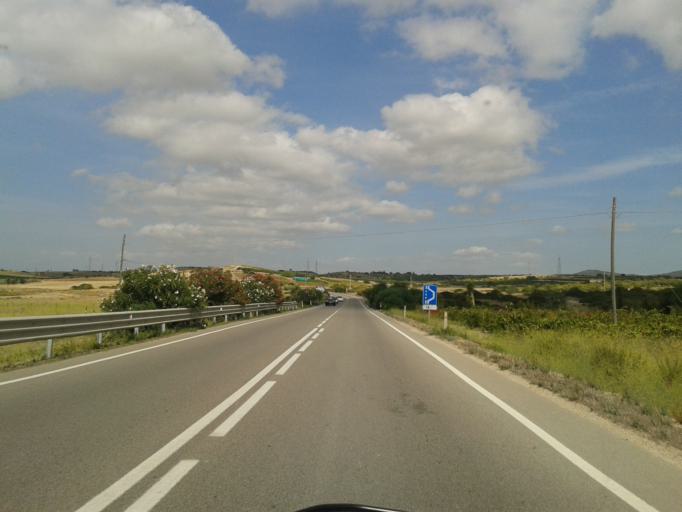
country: IT
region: Sardinia
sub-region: Provincia di Cagliari
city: Maracalagonis
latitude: 39.2647
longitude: 9.2190
